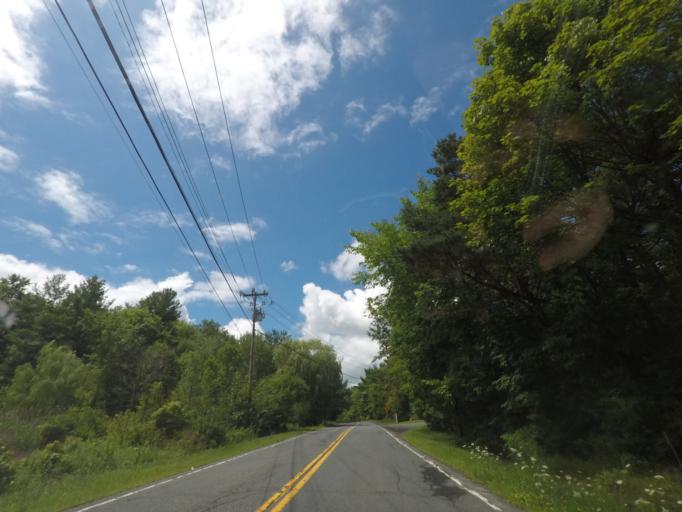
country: US
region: New York
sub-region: Rensselaer County
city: Wynantskill
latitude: 42.6686
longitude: -73.6452
